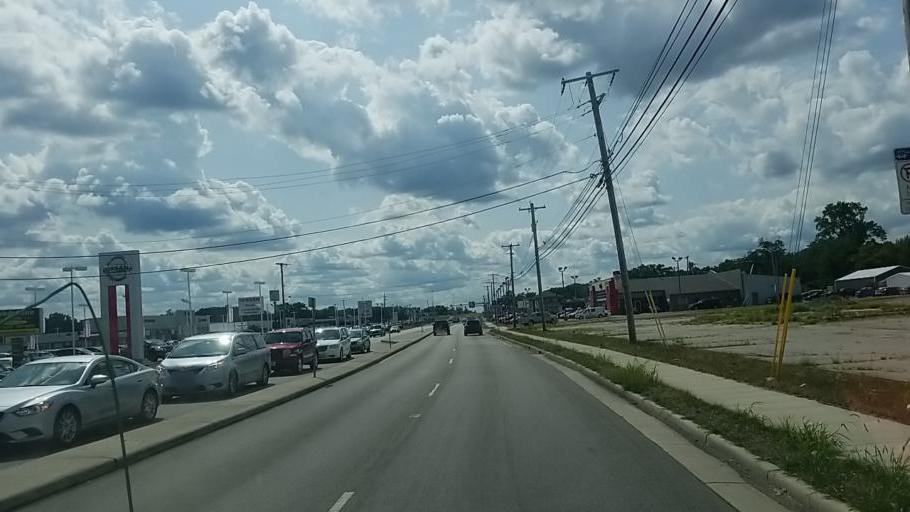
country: US
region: Ohio
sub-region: Lucas County
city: Ottawa Hills
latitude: 41.6763
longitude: -83.6839
